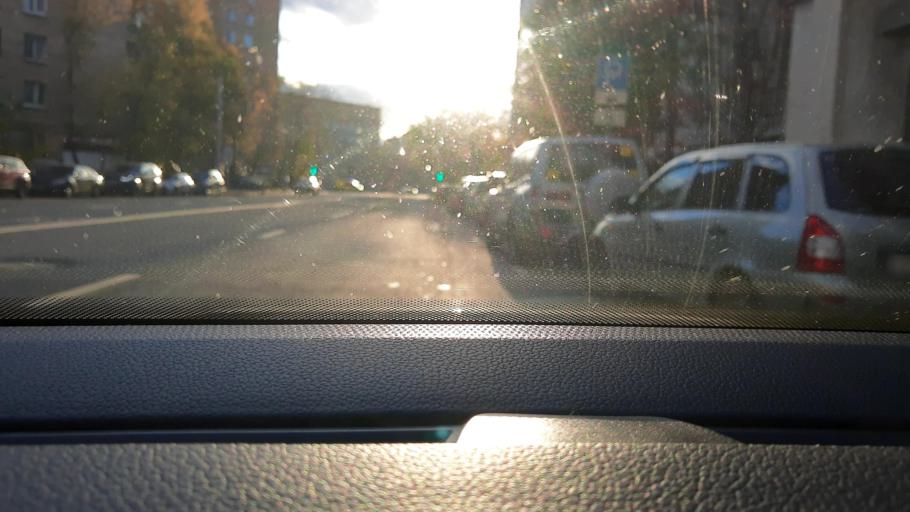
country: RU
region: Moskovskaya
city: Dorogomilovo
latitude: 55.7712
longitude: 37.5680
